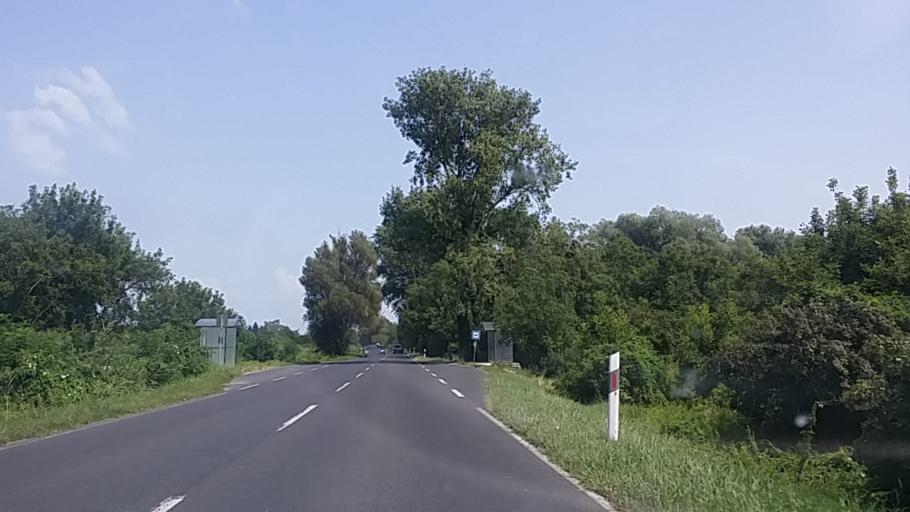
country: HU
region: Veszprem
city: Badacsonytomaj
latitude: 46.7856
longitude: 17.4877
